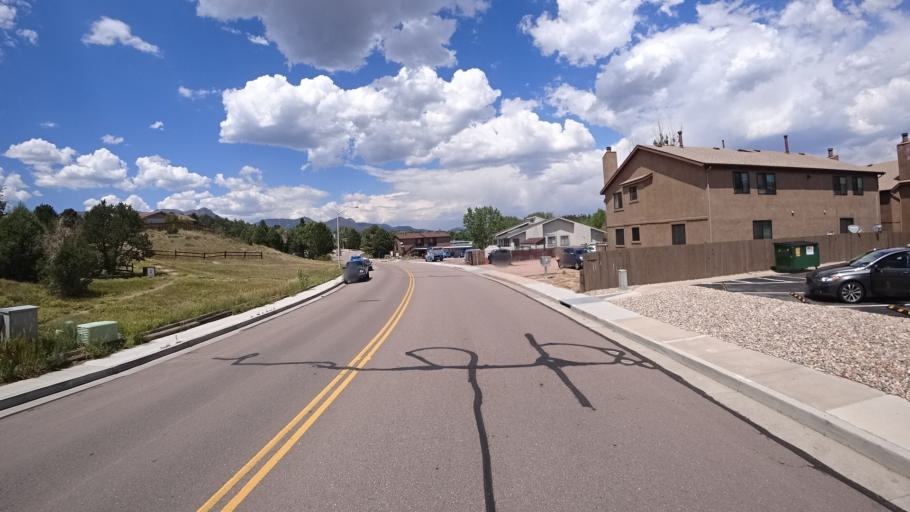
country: US
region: Colorado
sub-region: El Paso County
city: Air Force Academy
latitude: 38.9304
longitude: -104.8318
